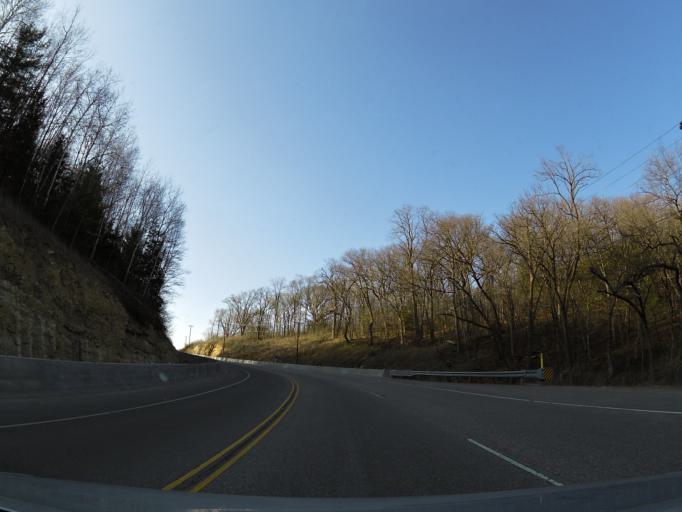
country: US
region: Minnesota
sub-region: Washington County
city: Afton
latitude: 44.8337
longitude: -92.7289
